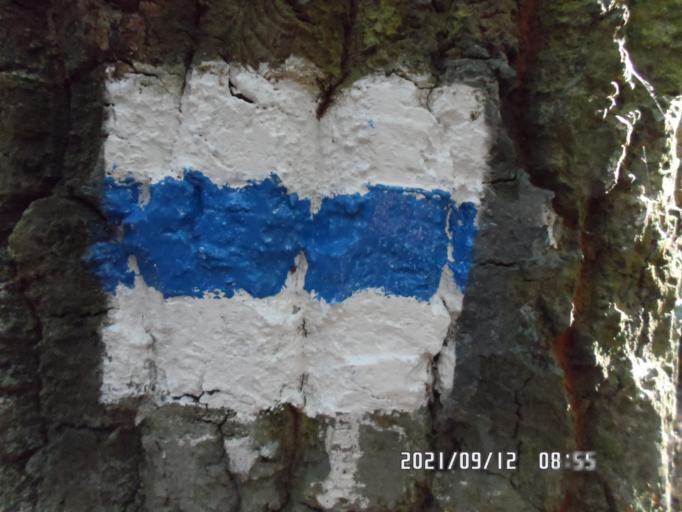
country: HU
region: Zala
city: Zalalovo
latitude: 46.7998
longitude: 16.6623
